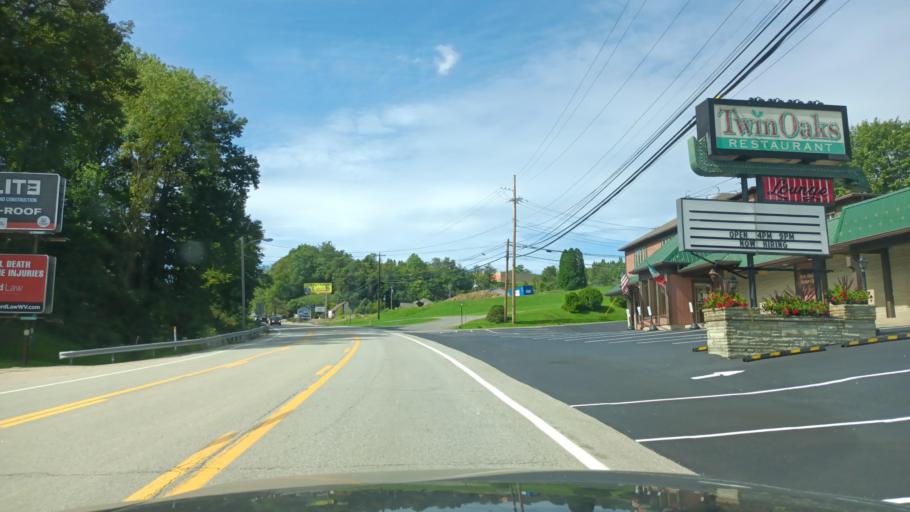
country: US
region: West Virginia
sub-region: Harrison County
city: Bridgeport
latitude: 39.2819
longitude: -80.2661
